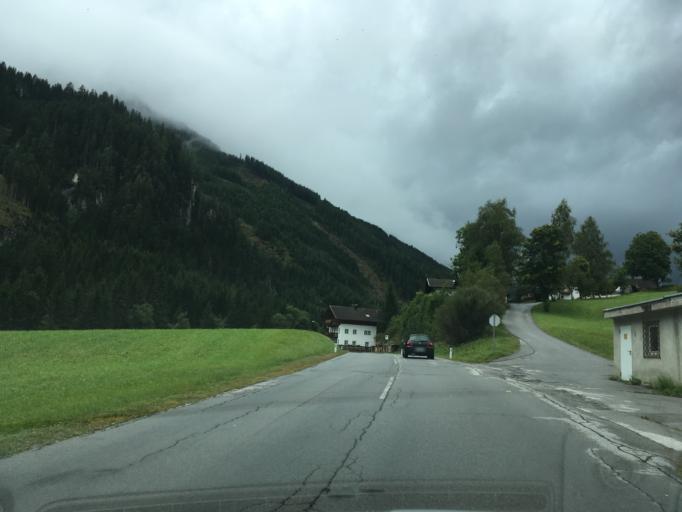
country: AT
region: Tyrol
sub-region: Politischer Bezirk Lienz
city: Virgen
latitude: 46.9186
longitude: 12.4100
